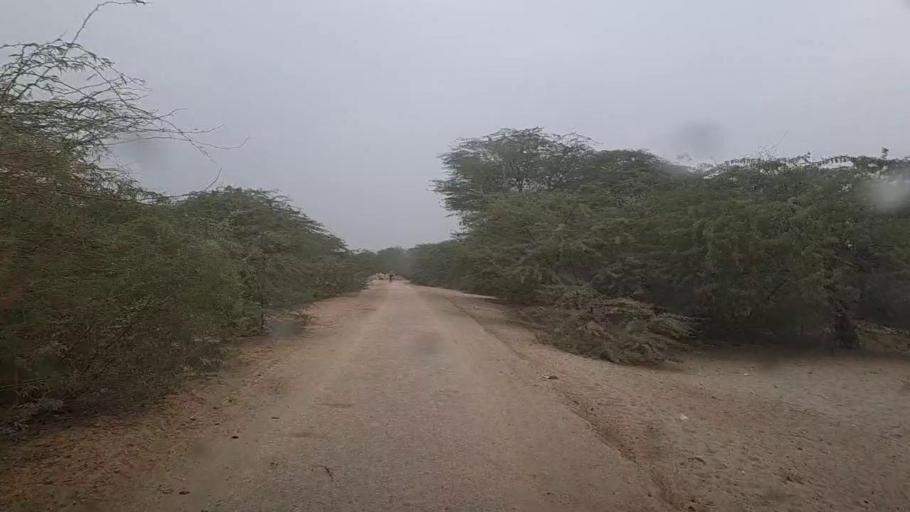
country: PK
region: Sindh
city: Gambat
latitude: 27.3544
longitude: 68.5991
